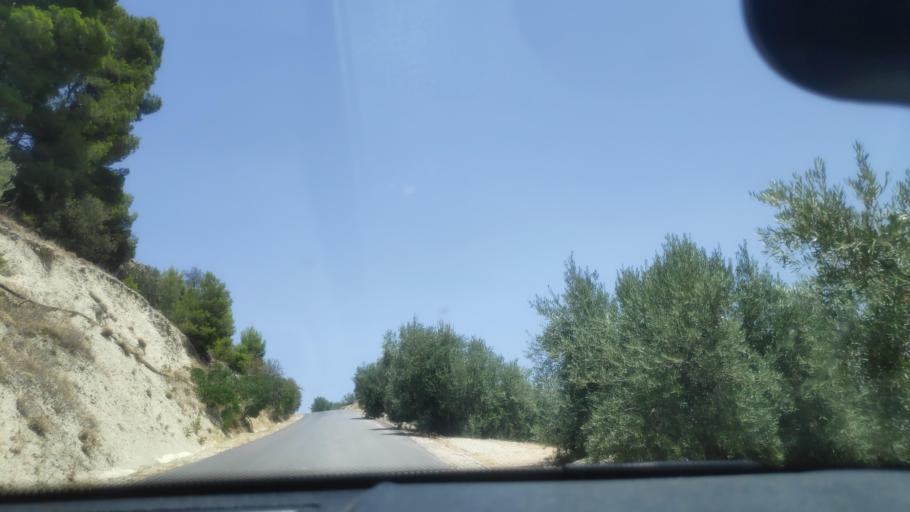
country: ES
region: Andalusia
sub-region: Provincia de Jaen
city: Torres
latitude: 37.7910
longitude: -3.4620
